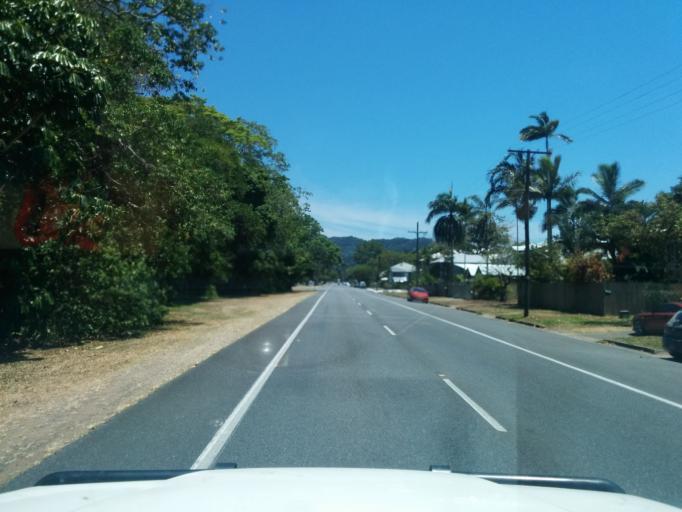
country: AU
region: Queensland
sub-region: Cairns
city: Cairns
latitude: -16.9173
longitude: 145.7579
